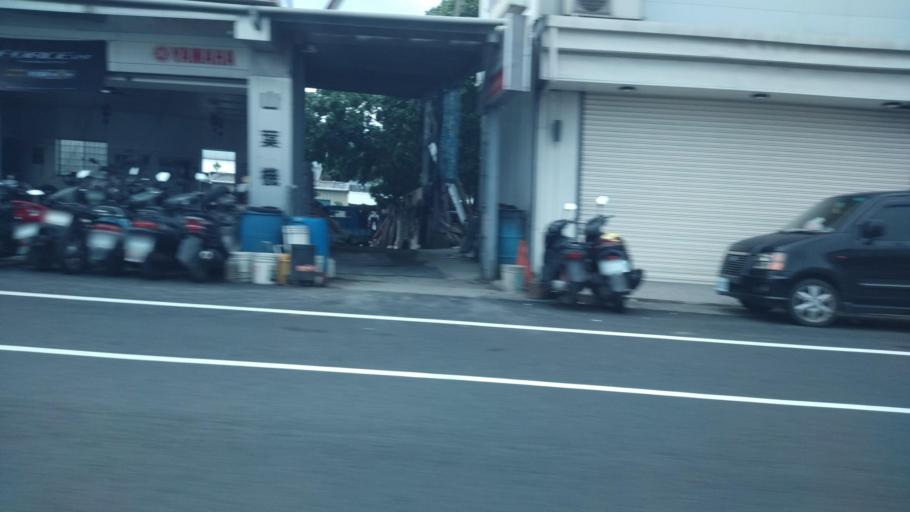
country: TW
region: Taiwan
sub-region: Hualien
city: Hualian
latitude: 24.0068
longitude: 121.6126
